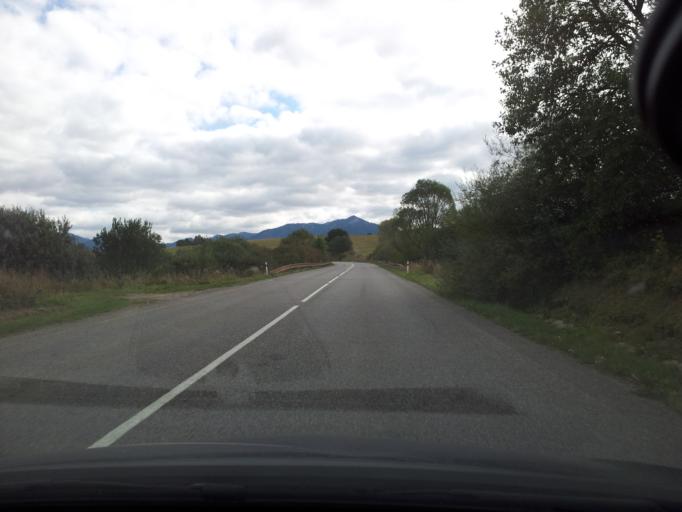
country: SK
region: Zilinsky
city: Ruzomberok
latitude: 49.0576
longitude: 19.4648
